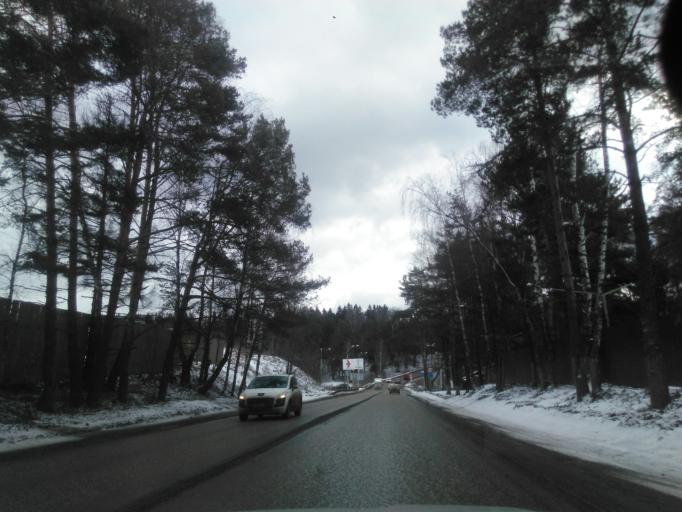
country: RU
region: Moskovskaya
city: Skhodnya
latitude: 55.8927
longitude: 37.2927
